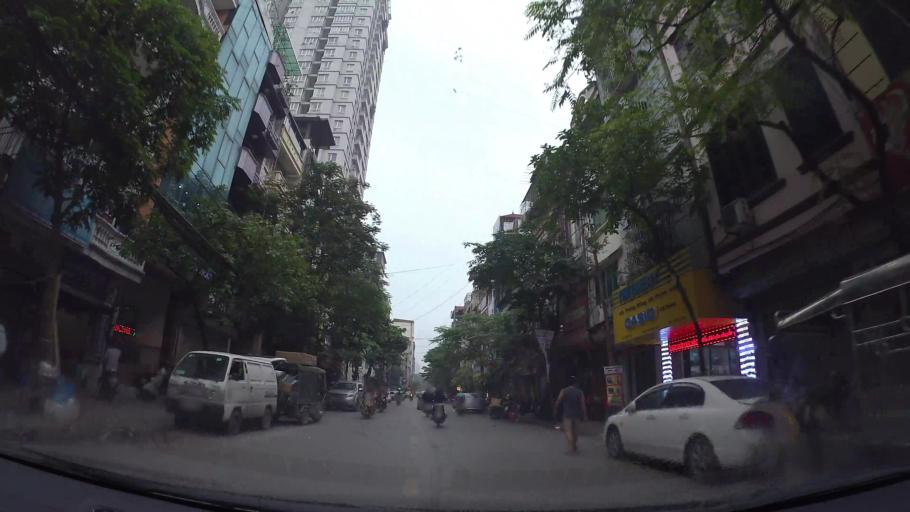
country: VN
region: Ha Noi
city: Hai BaTrung
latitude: 20.9980
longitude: 105.8424
